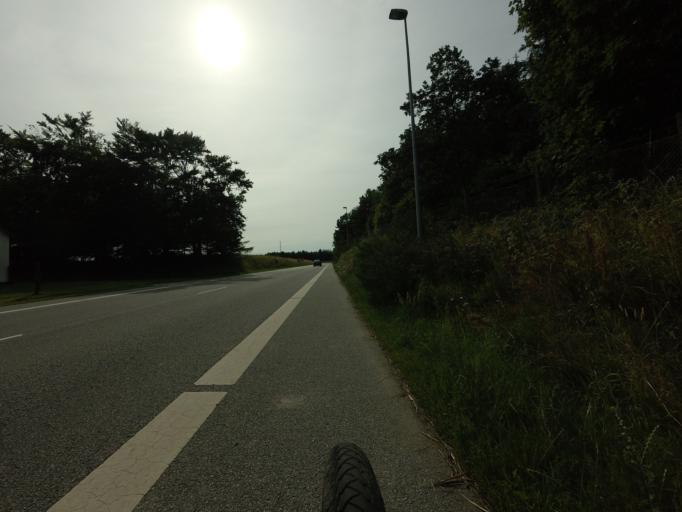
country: DK
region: North Denmark
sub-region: Hjorring Kommune
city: Hjorring
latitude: 57.4365
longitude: 9.9807
